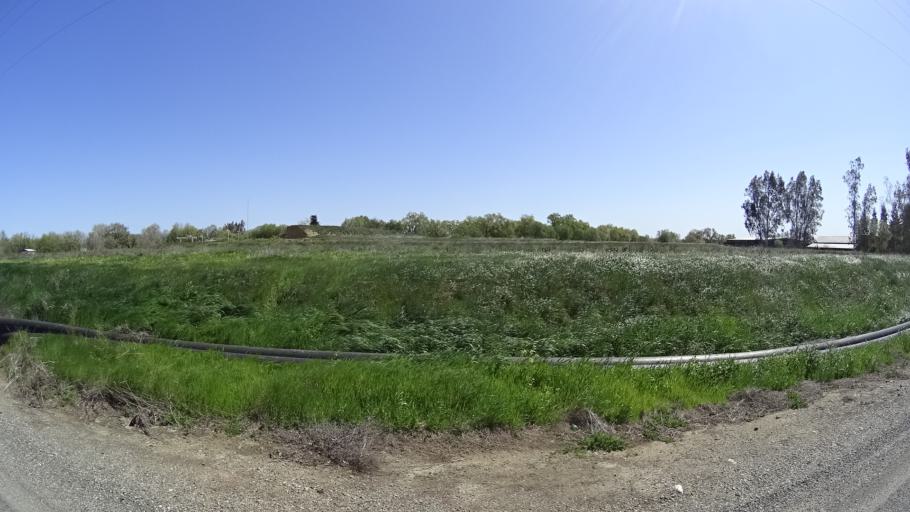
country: US
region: California
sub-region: Glenn County
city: Hamilton City
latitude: 39.7872
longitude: -122.0526
